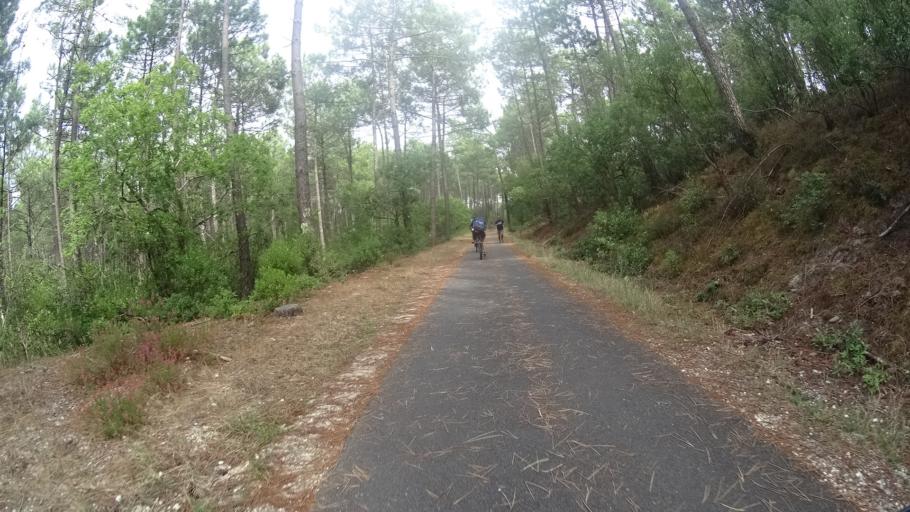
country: FR
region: Aquitaine
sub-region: Departement de la Gironde
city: Lacanau
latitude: 45.0075
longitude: -1.1464
